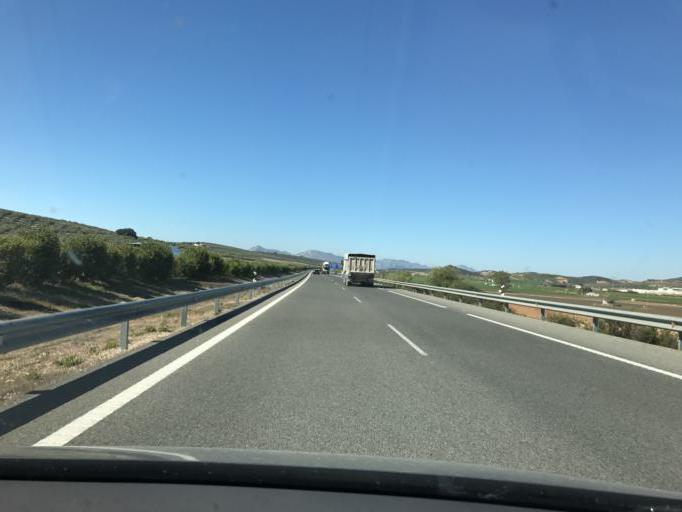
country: ES
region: Andalusia
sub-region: Provincia de Malaga
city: Villanueva del Trabuco
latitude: 37.0628
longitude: -4.3449
